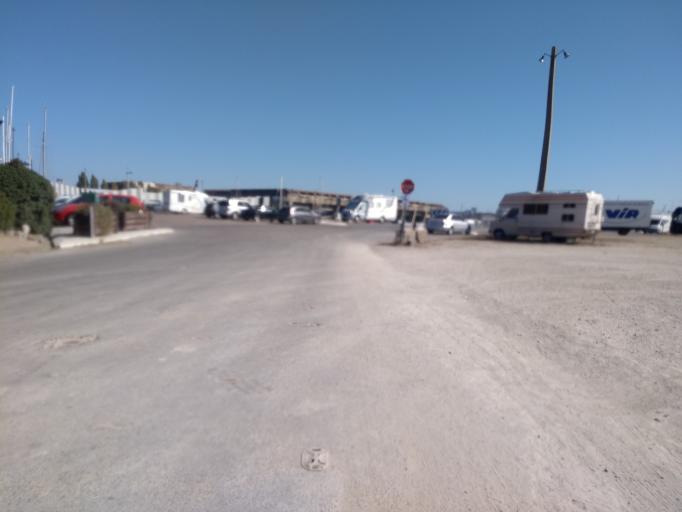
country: FR
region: Aquitaine
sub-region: Departement de la Gironde
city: Le Bouscat
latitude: 44.8697
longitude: -0.5654
